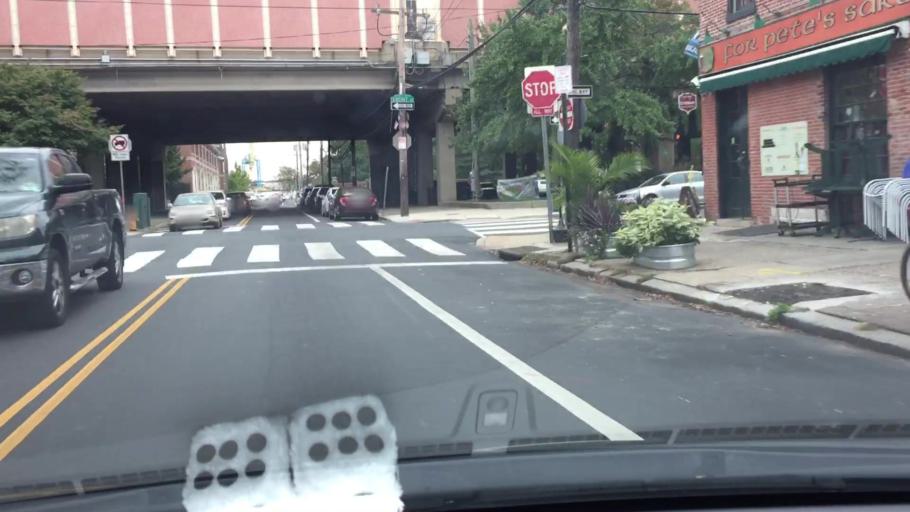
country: US
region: Pennsylvania
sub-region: Philadelphia County
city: Philadelphia
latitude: 39.9357
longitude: -75.1456
